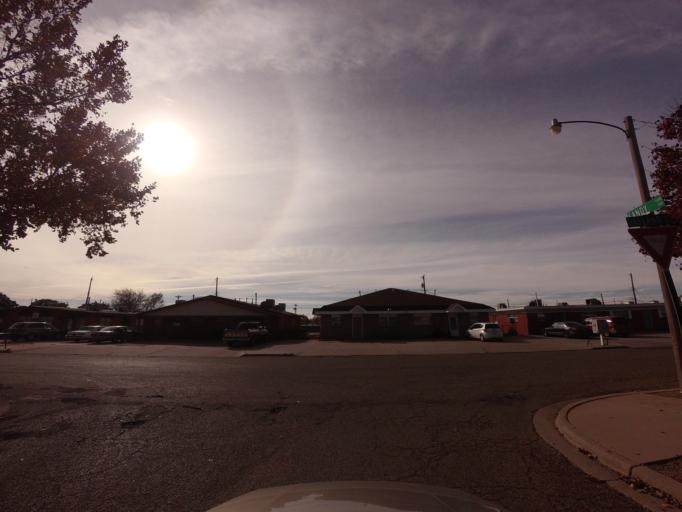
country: US
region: New Mexico
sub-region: Curry County
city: Clovis
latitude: 34.4211
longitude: -103.2245
